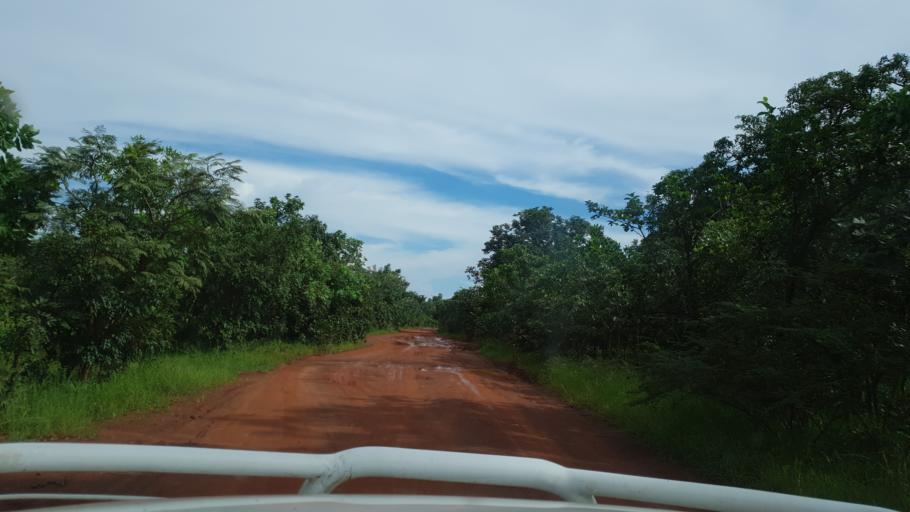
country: ML
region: Sikasso
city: Kolondieba
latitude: 10.7423
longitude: -6.9110
